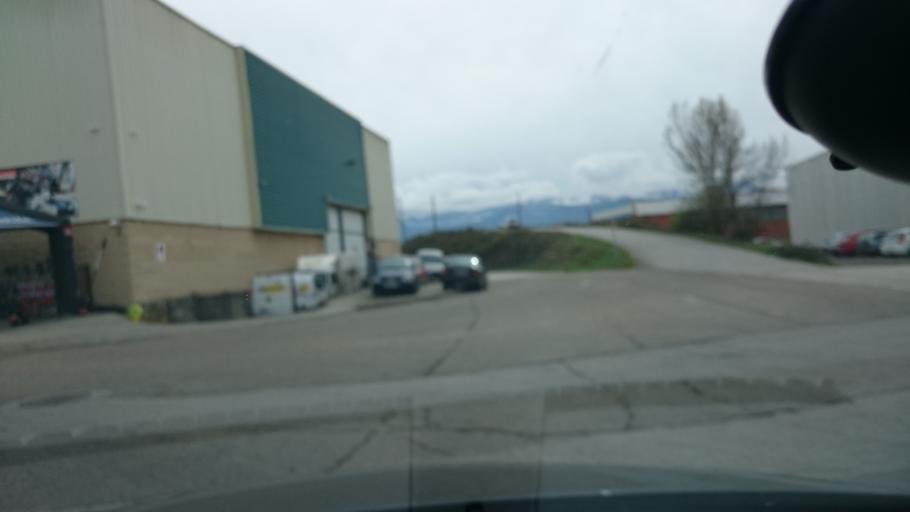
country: ES
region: Castille and Leon
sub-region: Provincia de Leon
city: Camponaraya
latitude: 42.5674
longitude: -6.6620
